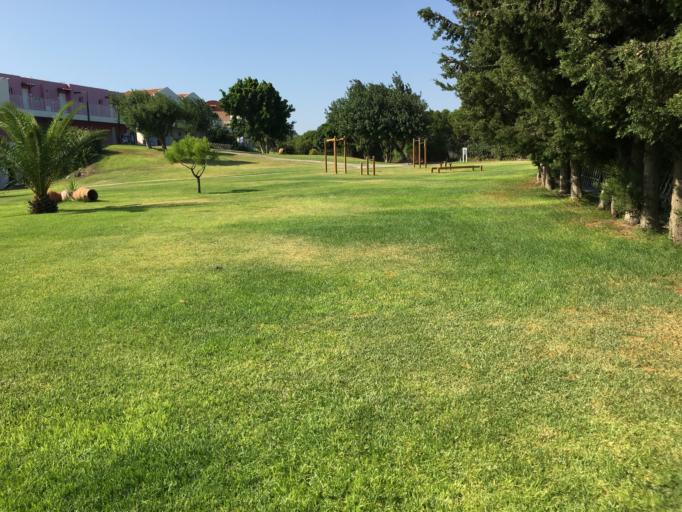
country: GR
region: South Aegean
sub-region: Nomos Dodekanisou
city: Rodos
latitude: 36.4063
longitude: 28.2258
